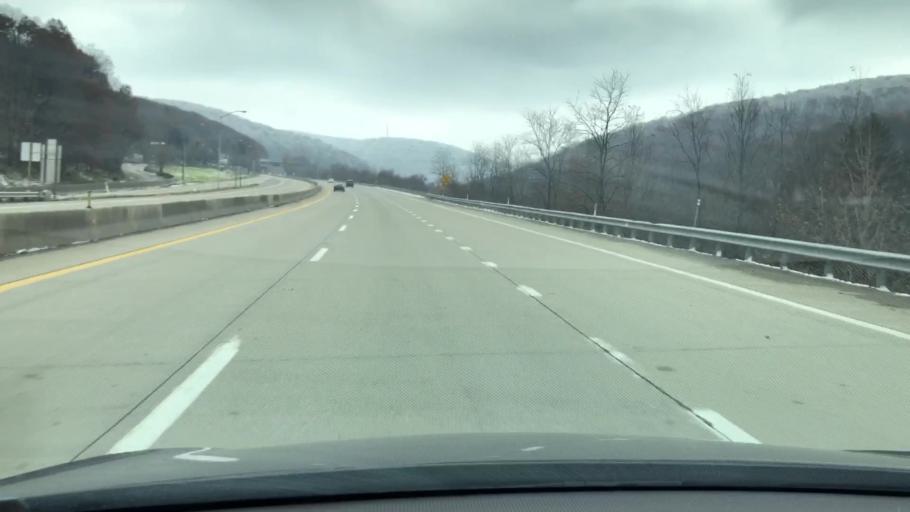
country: US
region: Pennsylvania
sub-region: Fayette County
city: Hopwood
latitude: 39.8687
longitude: -79.6964
